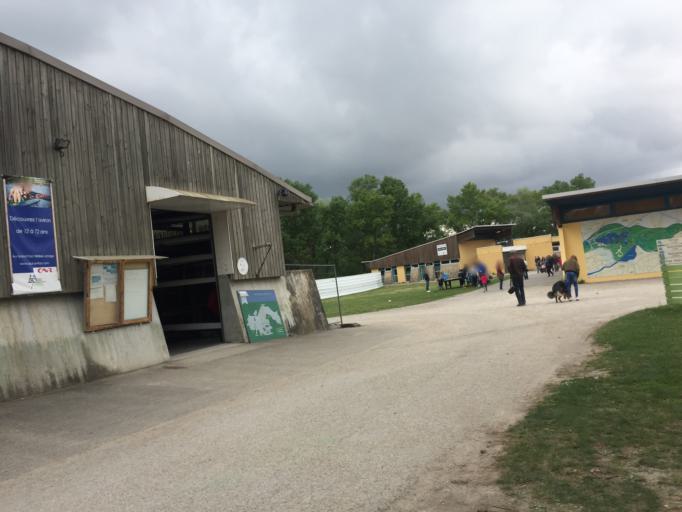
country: FR
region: Rhone-Alpes
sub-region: Departement du Rhone
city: Vaulx-en-Velin
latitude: 45.8002
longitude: 4.9404
